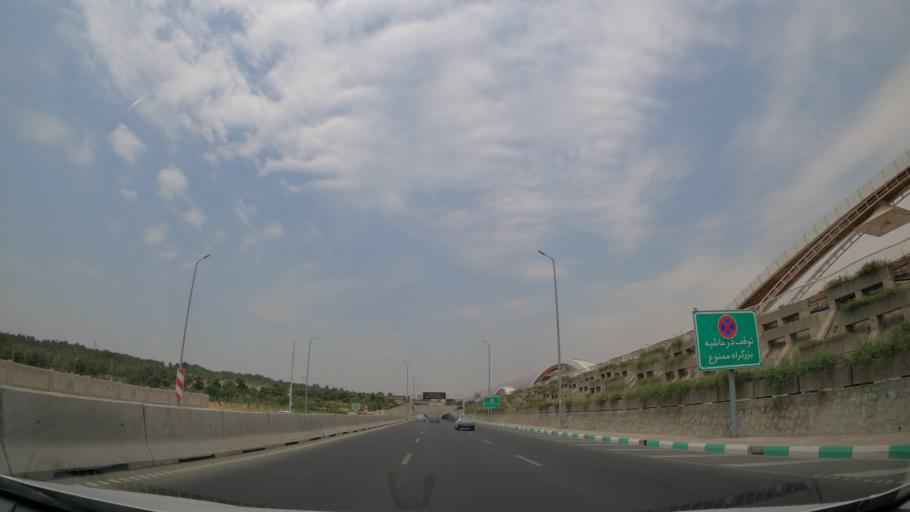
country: IR
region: Tehran
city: Shahr-e Qods
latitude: 35.7399
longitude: 51.2131
